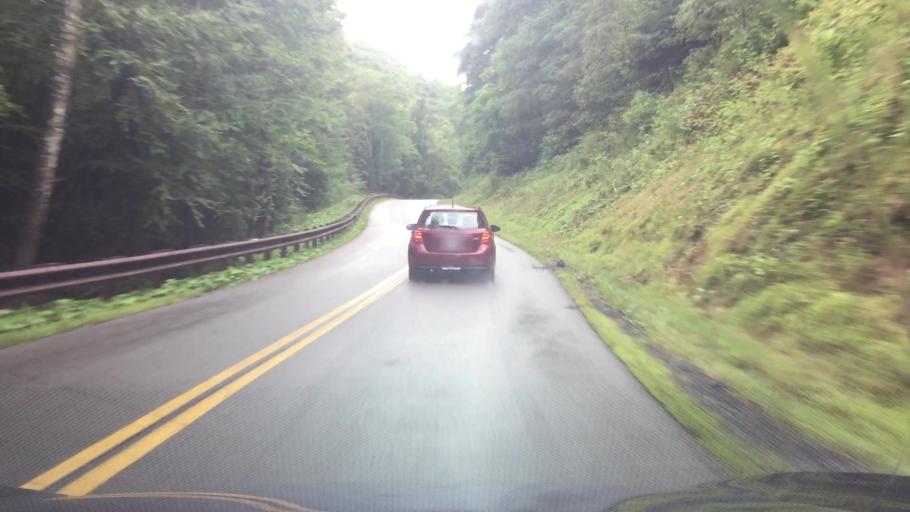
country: US
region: Virginia
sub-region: Smyth County
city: Atkins
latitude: 36.8340
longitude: -81.4165
